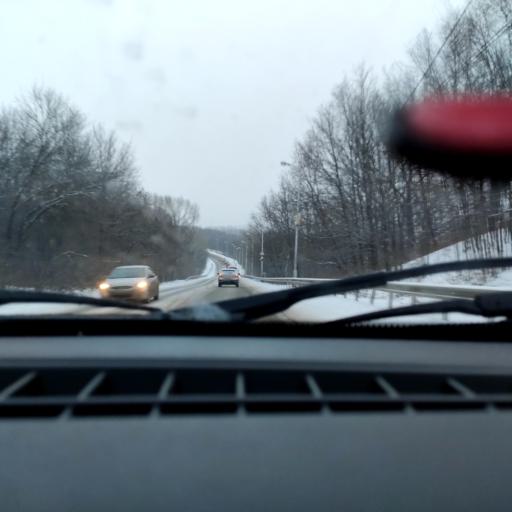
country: RU
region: Bashkortostan
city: Ufa
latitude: 54.8730
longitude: 56.0619
